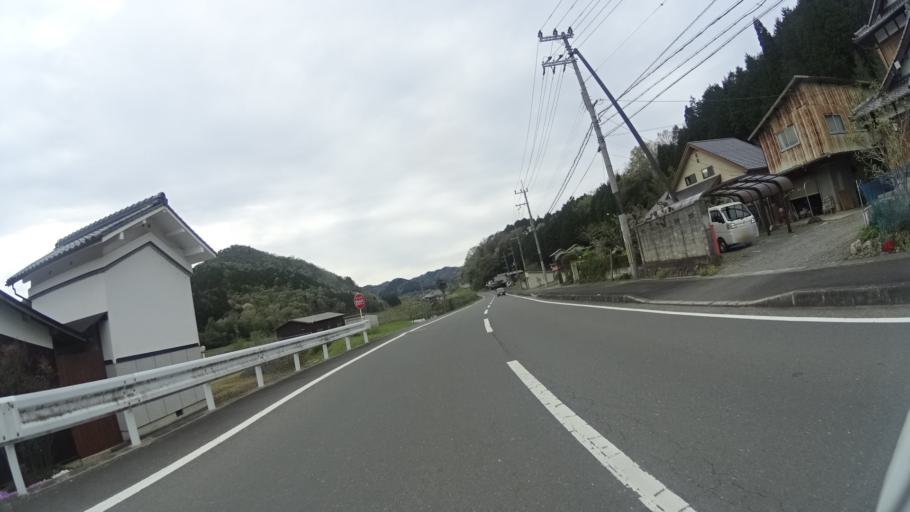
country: JP
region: Kyoto
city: Ayabe
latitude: 35.1803
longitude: 135.4372
